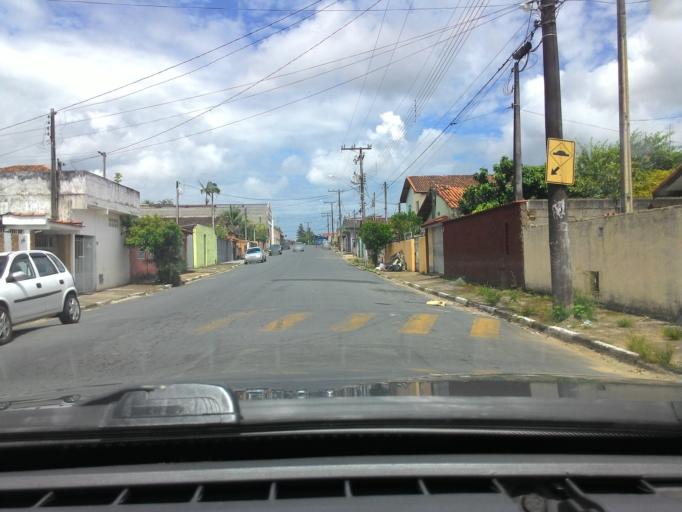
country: BR
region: Sao Paulo
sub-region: Registro
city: Registro
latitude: -24.5060
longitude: -47.8417
